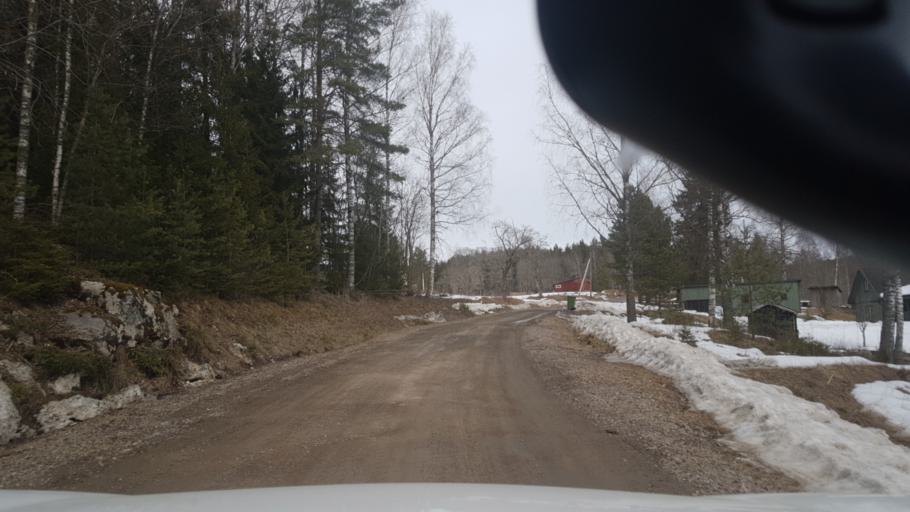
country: SE
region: Vaermland
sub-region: Eda Kommun
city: Amotfors
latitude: 59.8086
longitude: 12.4413
